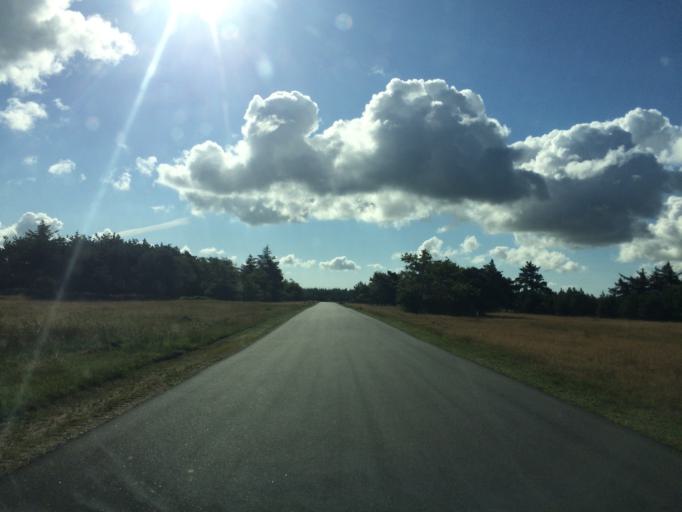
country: DK
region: South Denmark
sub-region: Varde Kommune
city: Oksbol
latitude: 55.6388
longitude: 8.1846
